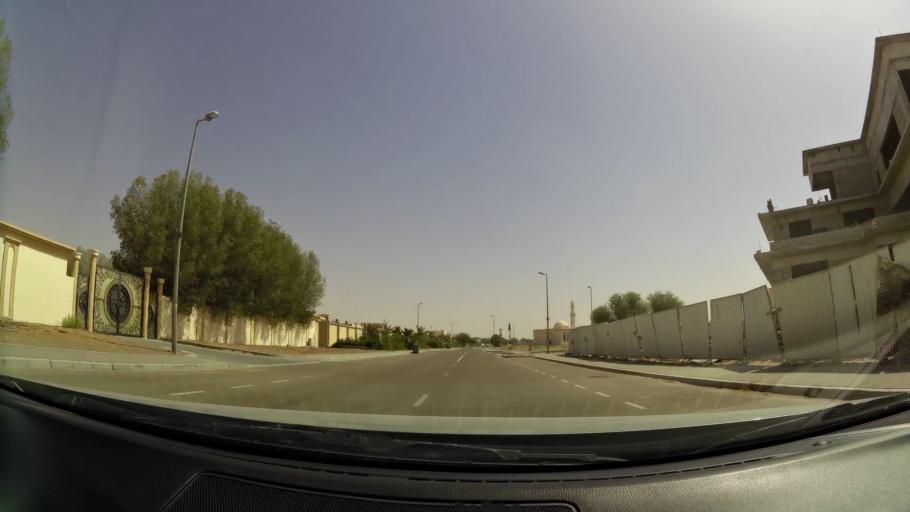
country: OM
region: Al Buraimi
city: Al Buraymi
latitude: 24.3078
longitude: 55.7482
